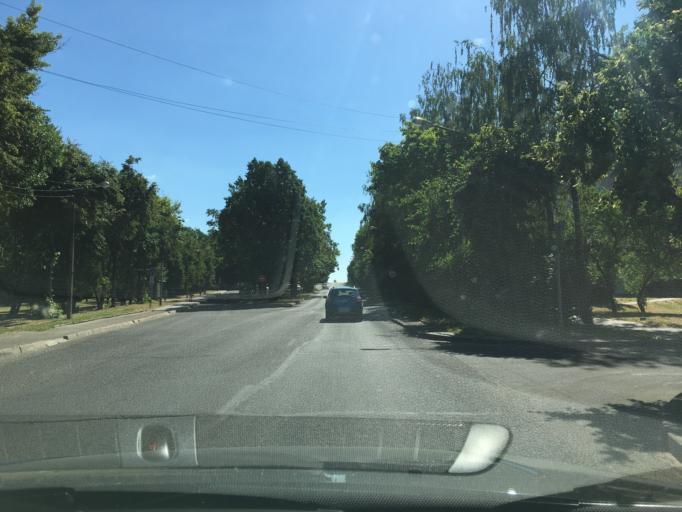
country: BY
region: Grodnenskaya
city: Hrodna
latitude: 53.6951
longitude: 23.8440
